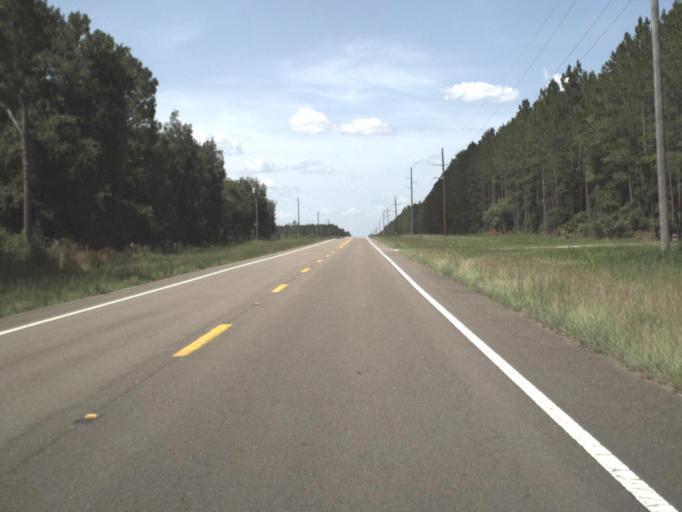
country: US
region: Florida
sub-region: Gilchrist County
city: Trenton
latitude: 29.6596
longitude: -82.7819
